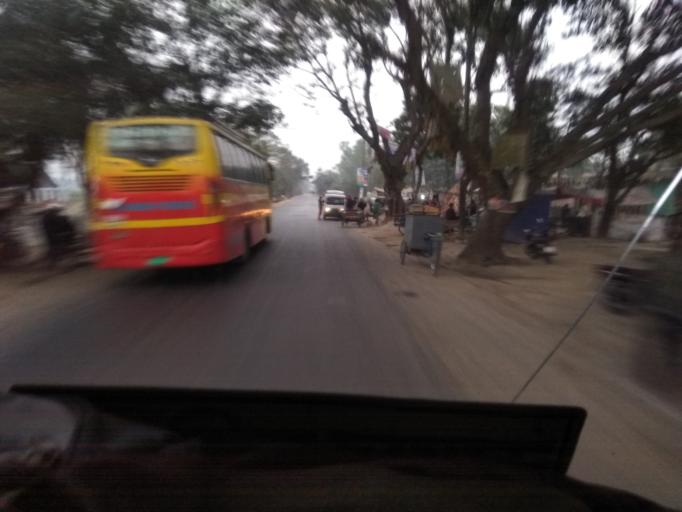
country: BD
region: Rajshahi
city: Bogra
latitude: 24.7365
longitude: 89.3293
